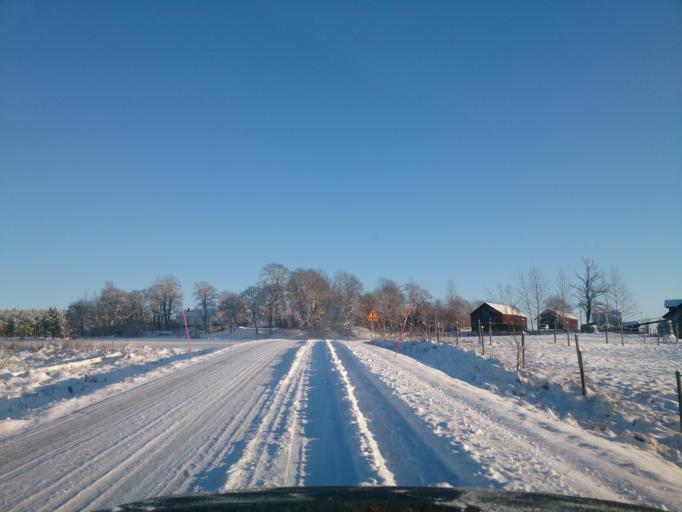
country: SE
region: OEstergoetland
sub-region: Norrkopings Kommun
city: Krokek
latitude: 58.5220
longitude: 16.4983
